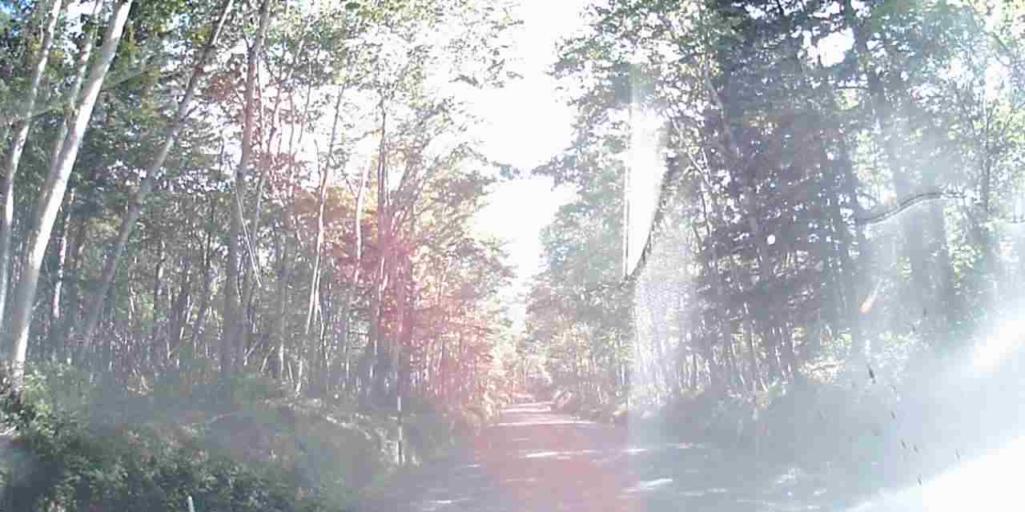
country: JP
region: Hokkaido
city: Shiraoi
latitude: 42.7051
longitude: 141.3946
